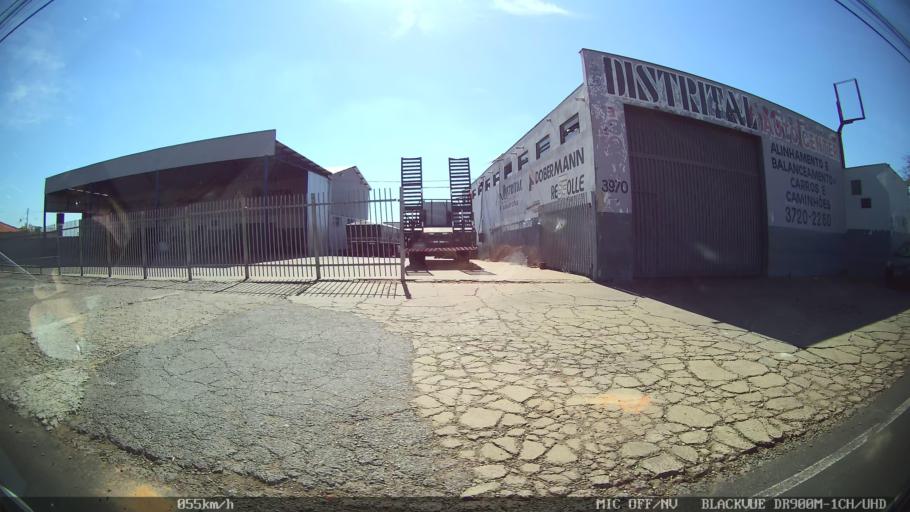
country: BR
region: Sao Paulo
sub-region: Franca
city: Franca
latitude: -20.5495
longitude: -47.4428
